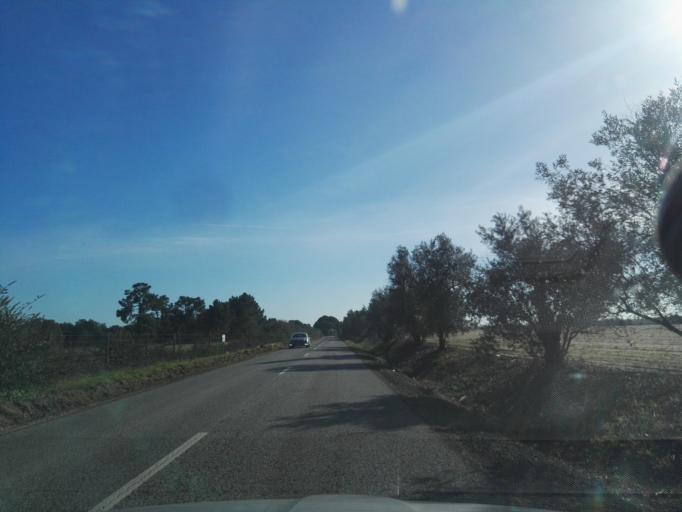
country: PT
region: Setubal
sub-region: Alcochete
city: Alcochete
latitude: 38.7314
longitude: -8.9222
